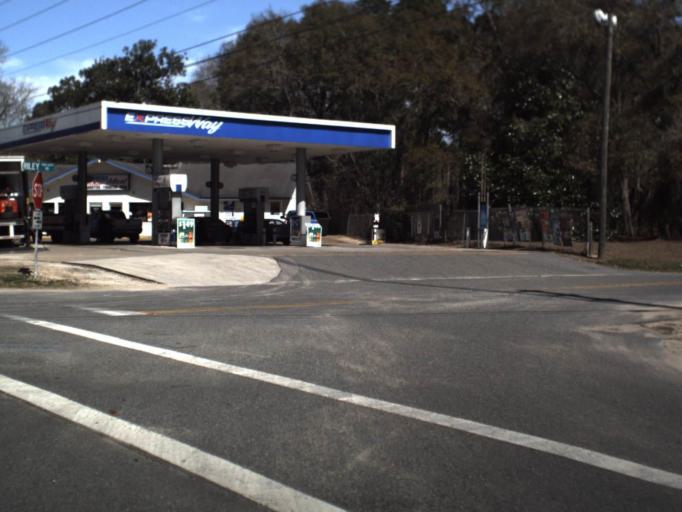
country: US
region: Florida
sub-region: Bay County
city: Lynn Haven
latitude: 30.2914
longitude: -85.6420
